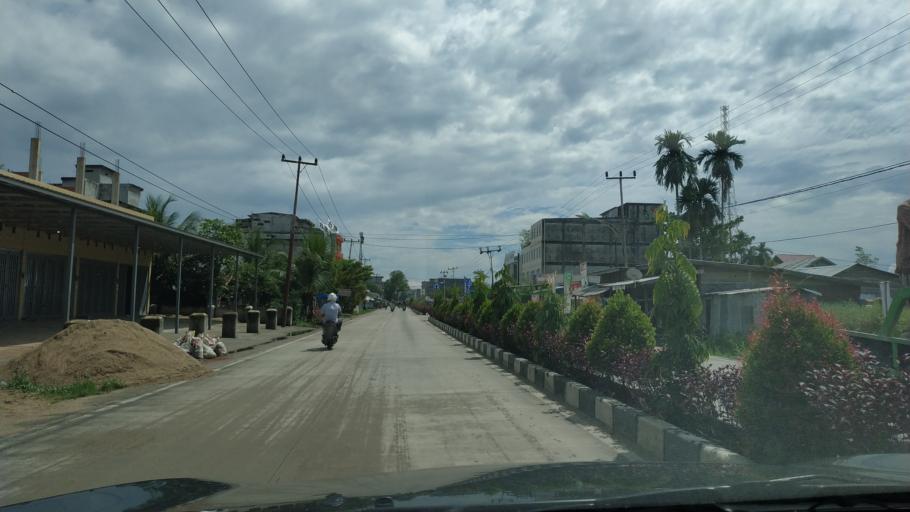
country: ID
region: Riau
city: Tembilahan
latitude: -0.3277
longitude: 103.1421
